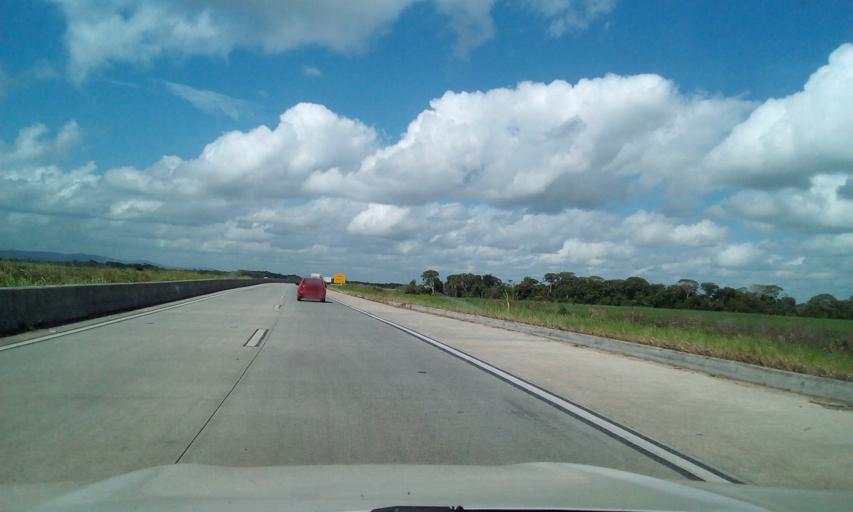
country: BR
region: Alagoas
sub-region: Messias
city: Messias
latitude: -9.3818
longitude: -35.8290
